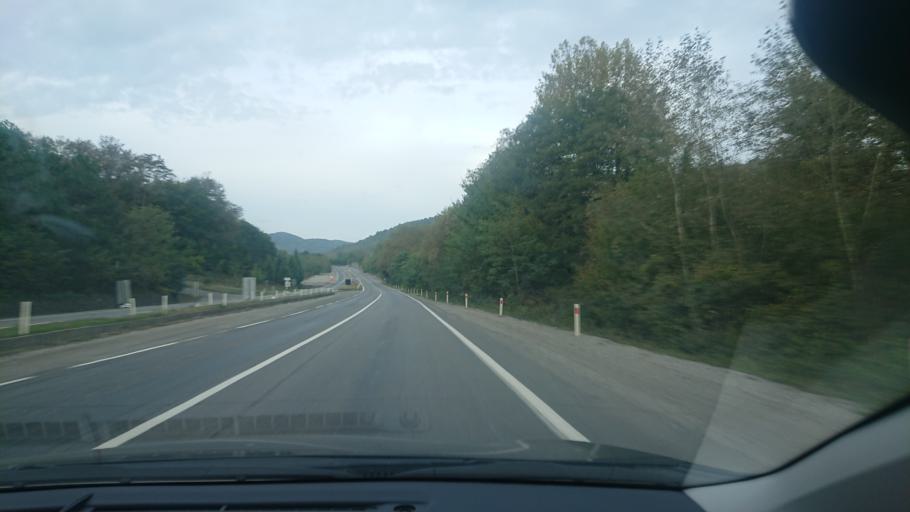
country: TR
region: Zonguldak
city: Beycuma
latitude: 41.3667
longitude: 31.9971
